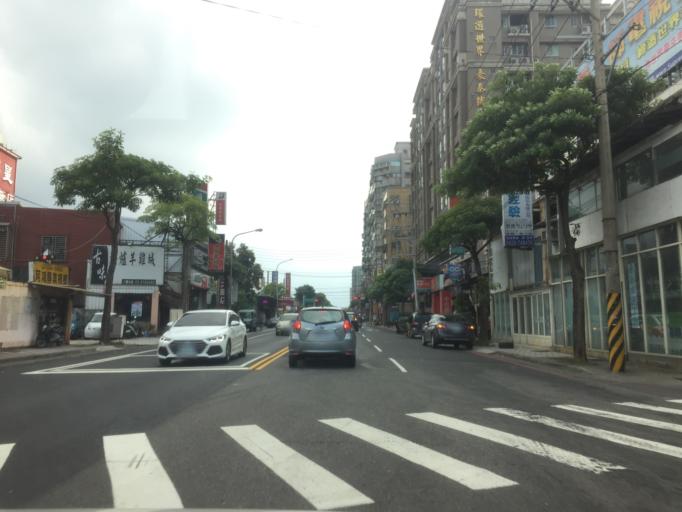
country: TW
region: Taiwan
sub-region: Taoyuan
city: Taoyuan
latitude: 24.9645
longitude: 121.3068
